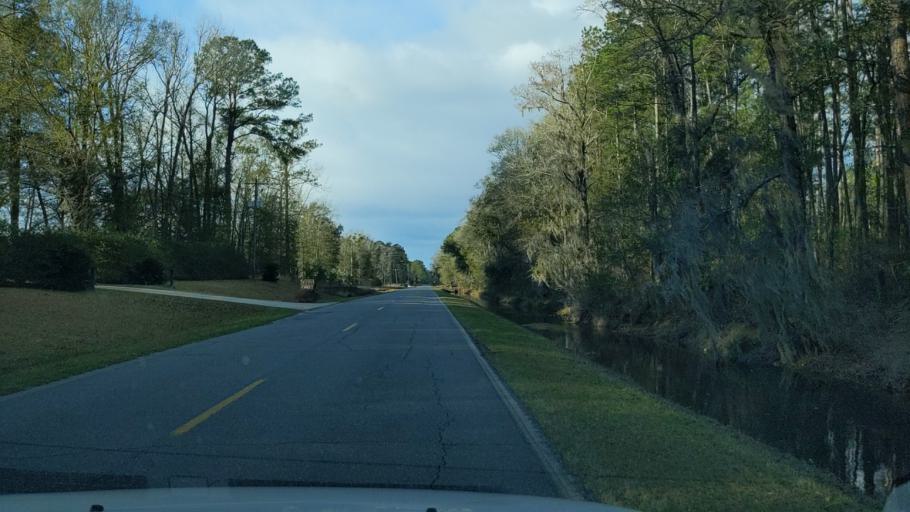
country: US
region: Georgia
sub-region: Chatham County
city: Pooler
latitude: 32.0403
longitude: -81.2983
